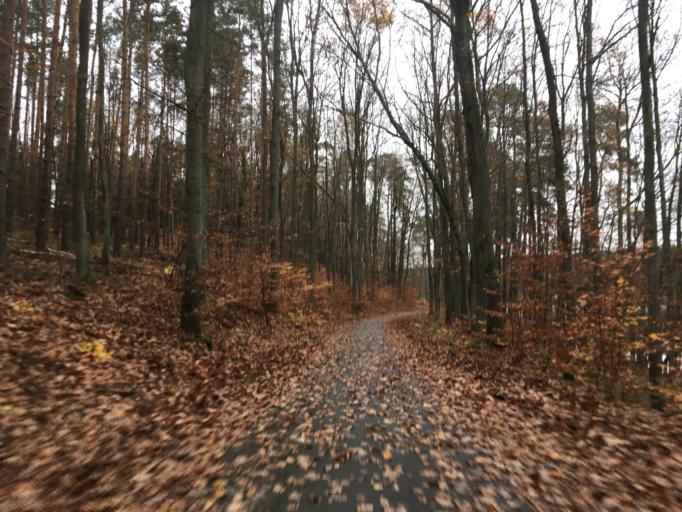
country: DE
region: Brandenburg
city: Mixdorf
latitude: 52.1575
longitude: 14.4429
